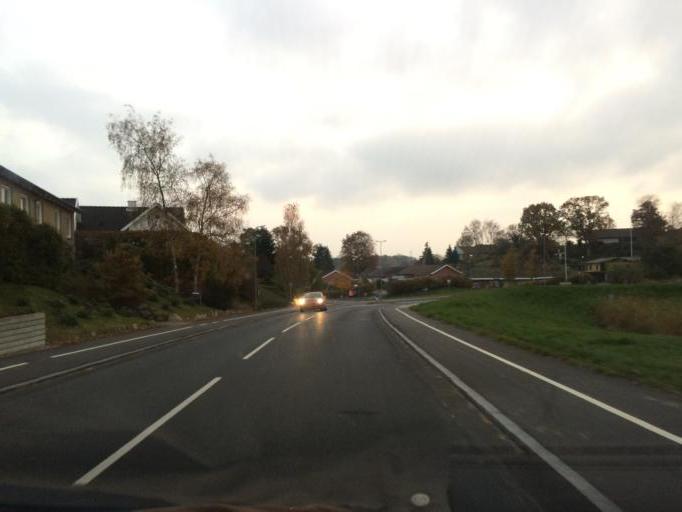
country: DK
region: Central Jutland
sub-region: Silkeborg Kommune
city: Silkeborg
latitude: 56.1800
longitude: 9.5201
